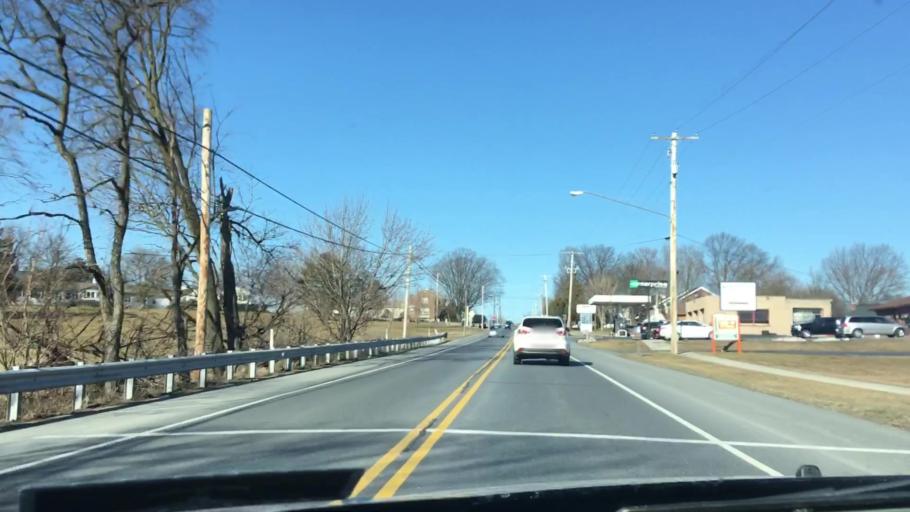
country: US
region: Pennsylvania
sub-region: Lancaster County
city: Akron
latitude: 40.1523
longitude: -76.2073
